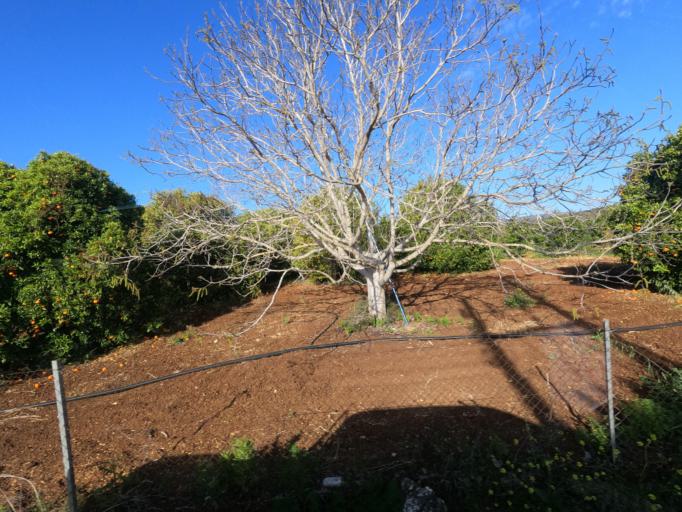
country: CY
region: Pafos
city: Polis
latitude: 35.0352
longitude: 32.3776
